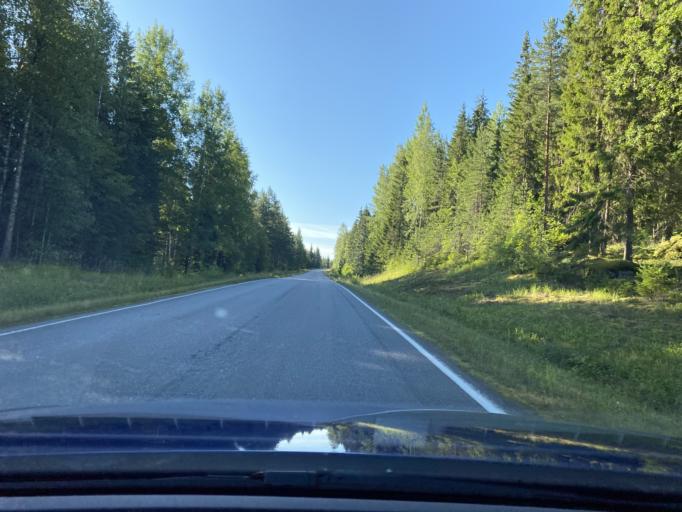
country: FI
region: Haeme
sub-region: Forssa
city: Tammela
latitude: 60.9416
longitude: 23.7739
